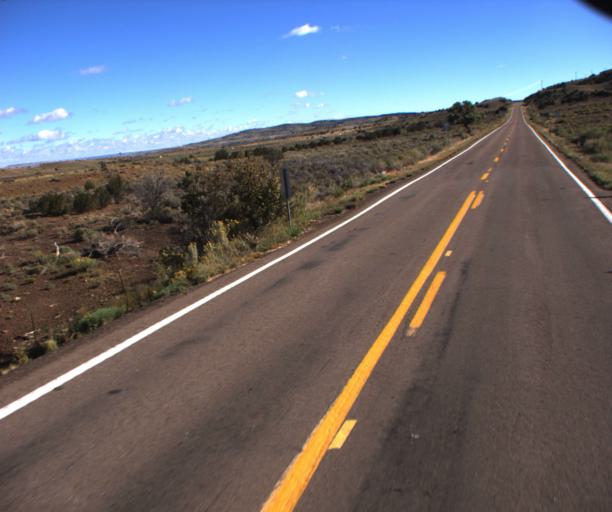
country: US
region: Arizona
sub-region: Apache County
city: Saint Johns
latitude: 34.4760
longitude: -109.6016
